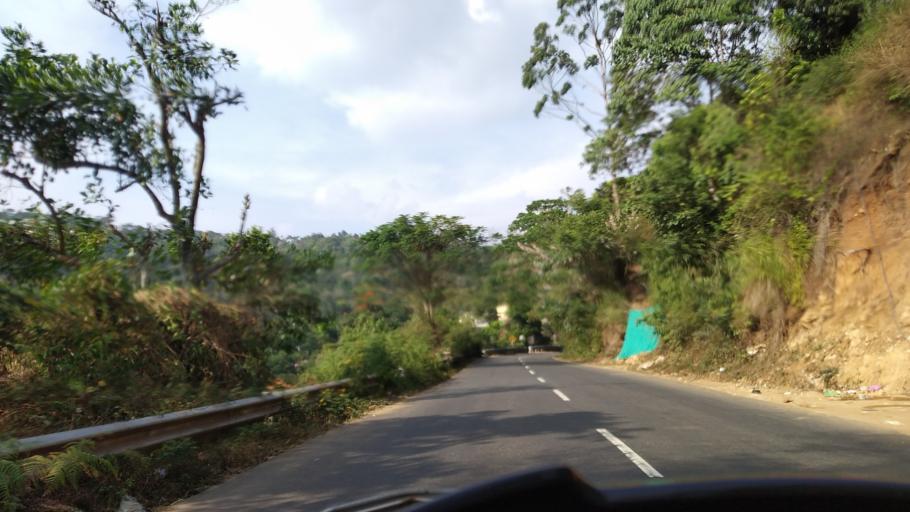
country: IN
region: Tamil Nadu
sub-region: Theni
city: Gudalur
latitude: 9.5728
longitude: 77.0555
